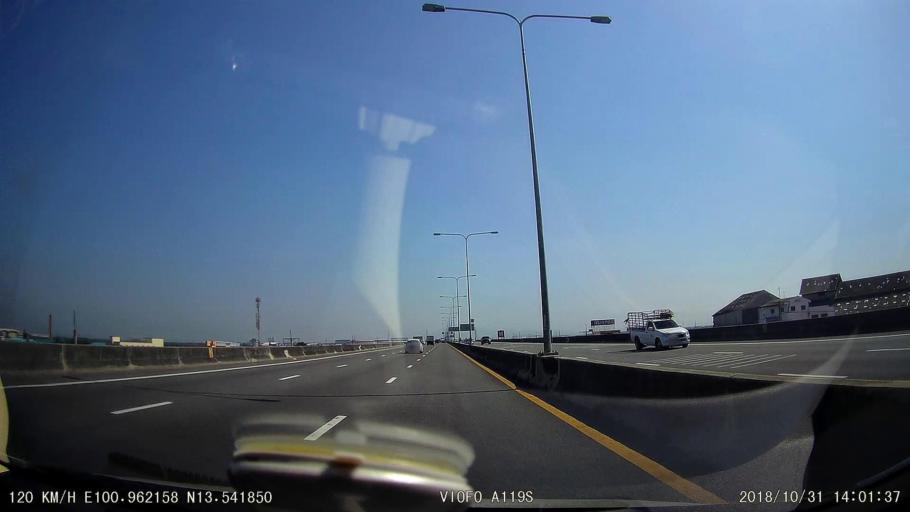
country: TH
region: Chachoengsao
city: Bang Pakong
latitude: 13.5414
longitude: 100.9623
